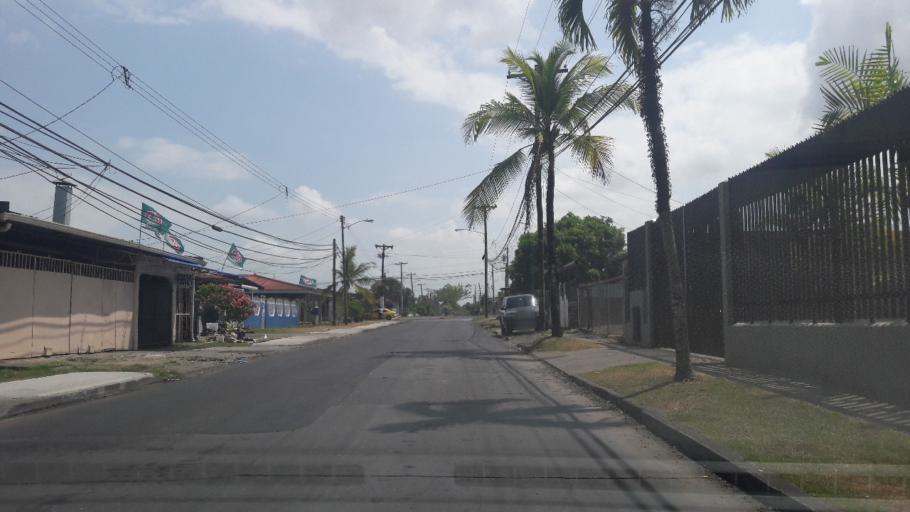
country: PA
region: Panama
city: Alcalde Diaz
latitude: 9.1335
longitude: -79.5494
